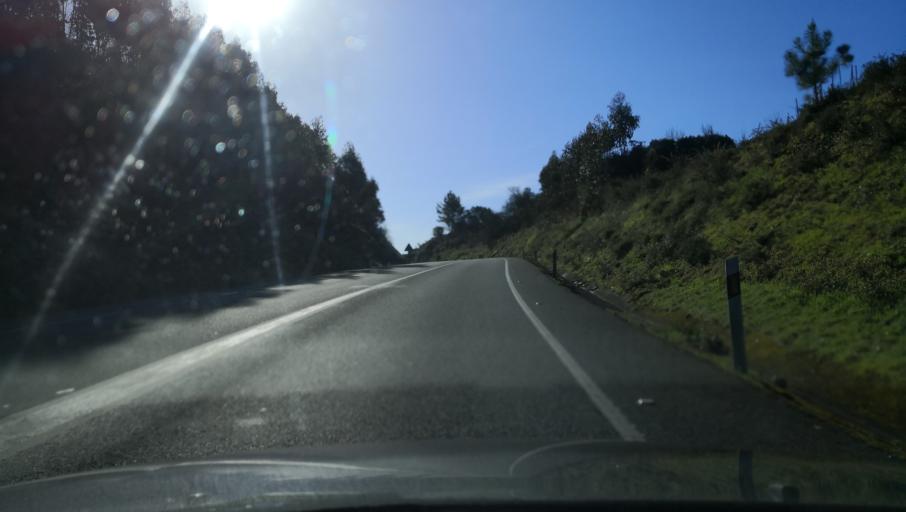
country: ES
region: Galicia
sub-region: Provincia da Coruna
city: Vedra
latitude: 42.7898
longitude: -8.4433
